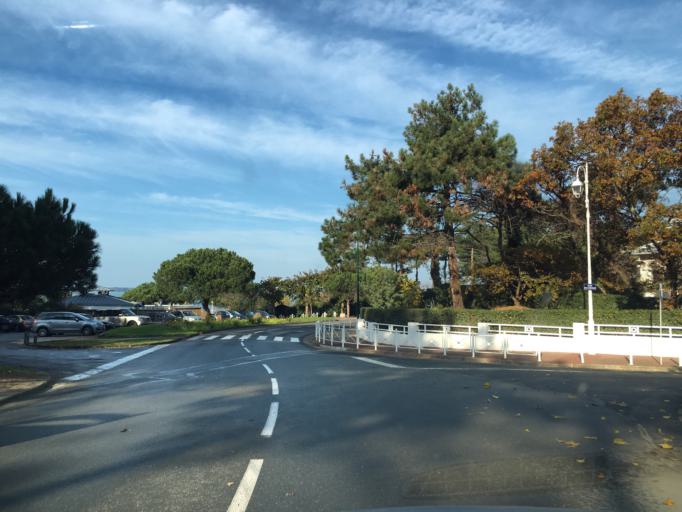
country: FR
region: Aquitaine
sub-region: Departement de la Gironde
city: Arcachon
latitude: 44.6523
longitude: -1.1942
